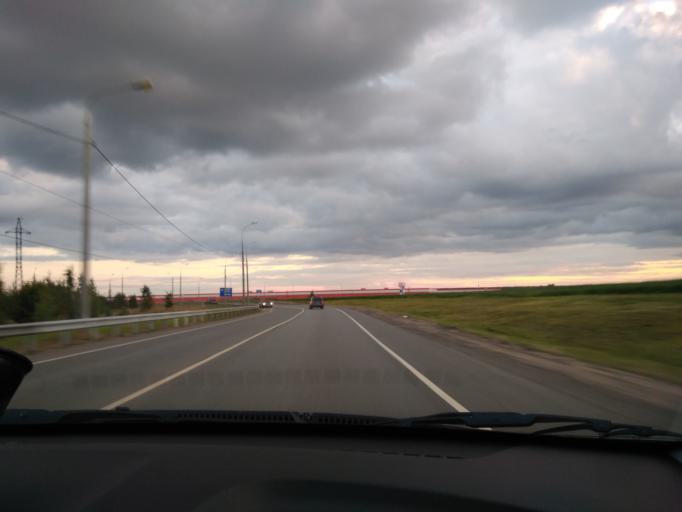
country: RU
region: Moskovskaya
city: Ramenskoye
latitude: 55.4892
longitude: 38.1533
